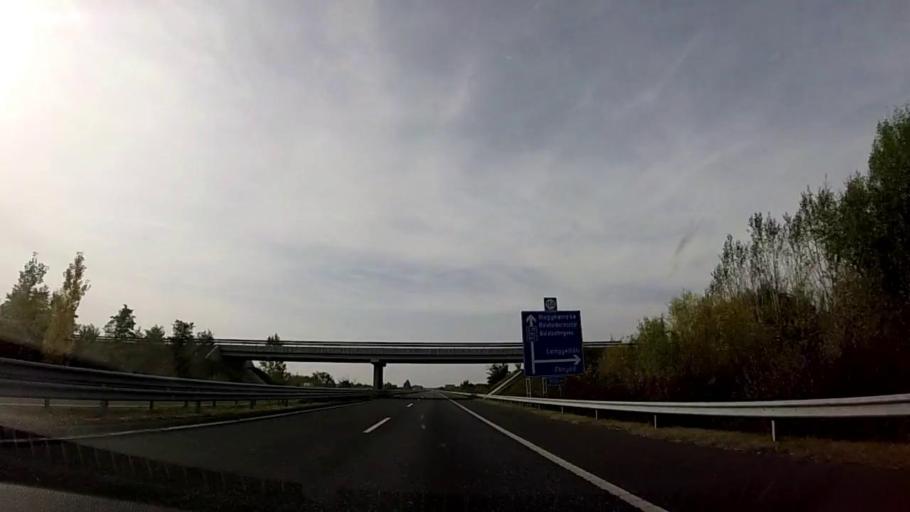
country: HU
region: Somogy
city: Fonyod
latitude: 46.7340
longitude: 17.5974
